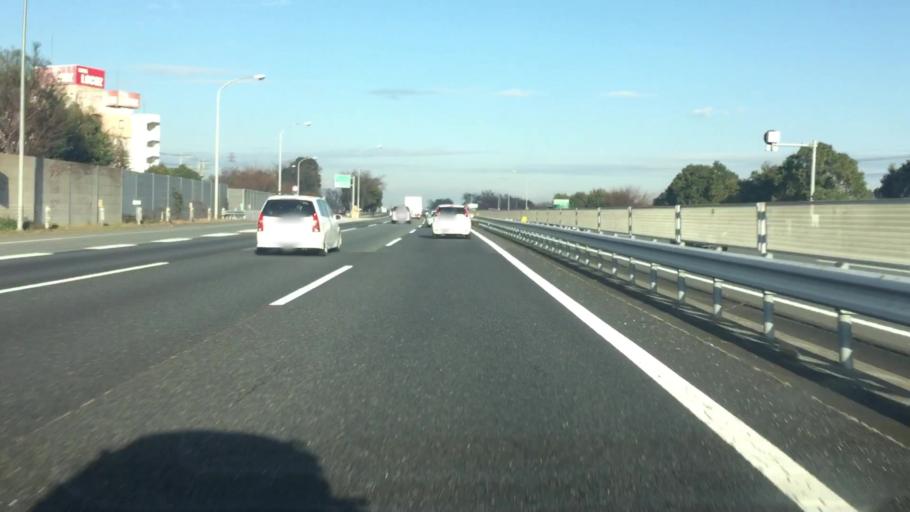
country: JP
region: Saitama
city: Honjo
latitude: 36.2158
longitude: 139.1664
